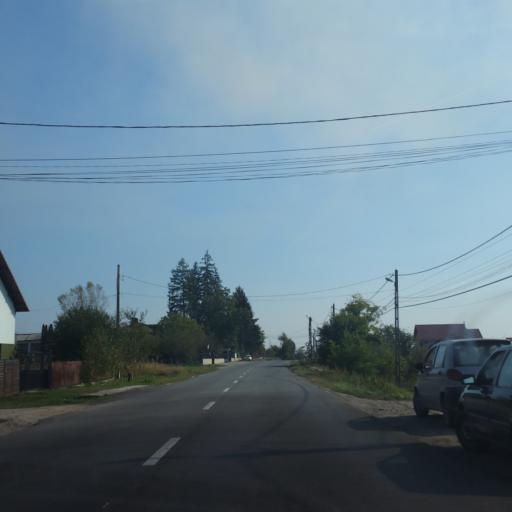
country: RO
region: Arges
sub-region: Comuna Baiculesti
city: Baiculesti
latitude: 45.0831
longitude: 24.6803
